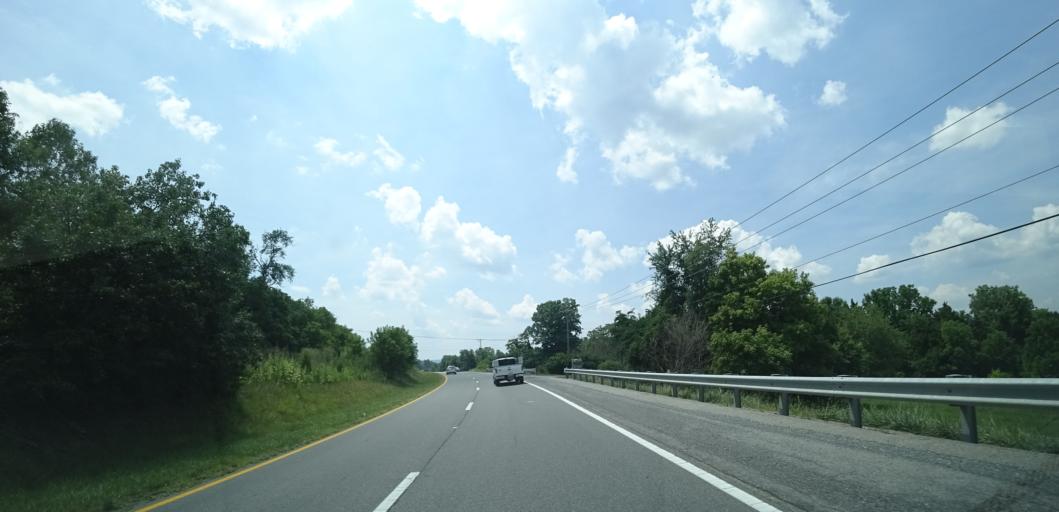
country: US
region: Virginia
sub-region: Botetourt County
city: Daleville
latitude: 37.4438
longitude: -79.9047
